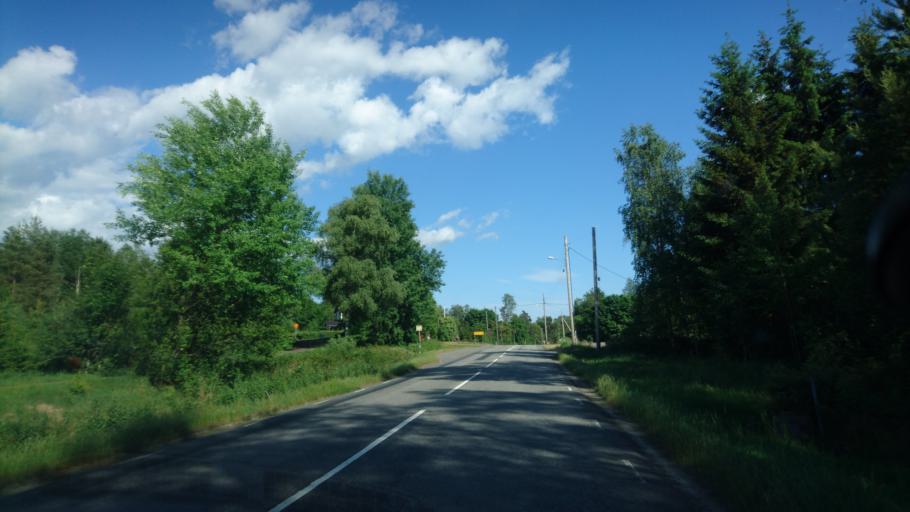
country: SE
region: Kronoberg
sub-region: Almhults Kommun
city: AElmhult
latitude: 56.4759
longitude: 14.2169
